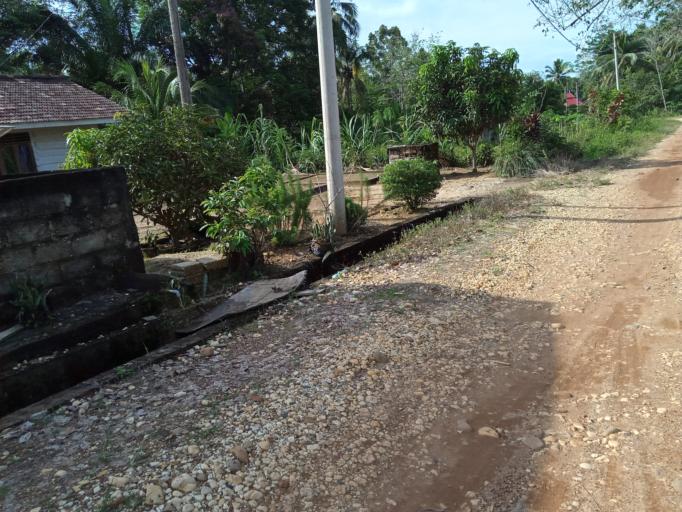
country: ID
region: Jambi
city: Muaralimun
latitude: -2.4368
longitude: 102.7384
